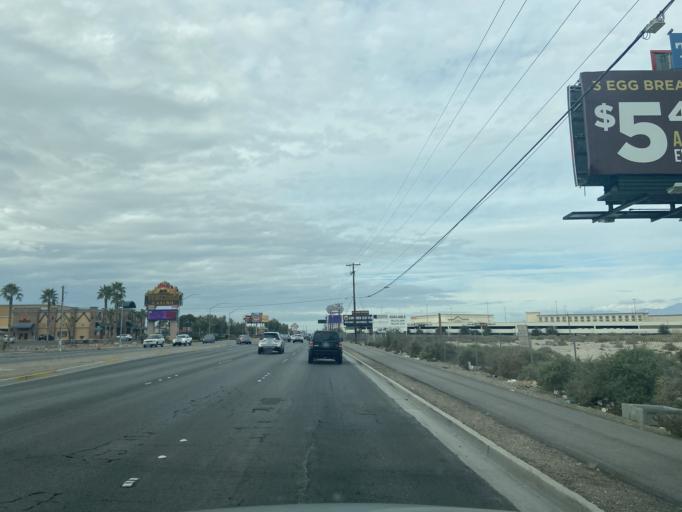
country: US
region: Nevada
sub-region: Clark County
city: Las Vegas
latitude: 36.1932
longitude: -115.1901
